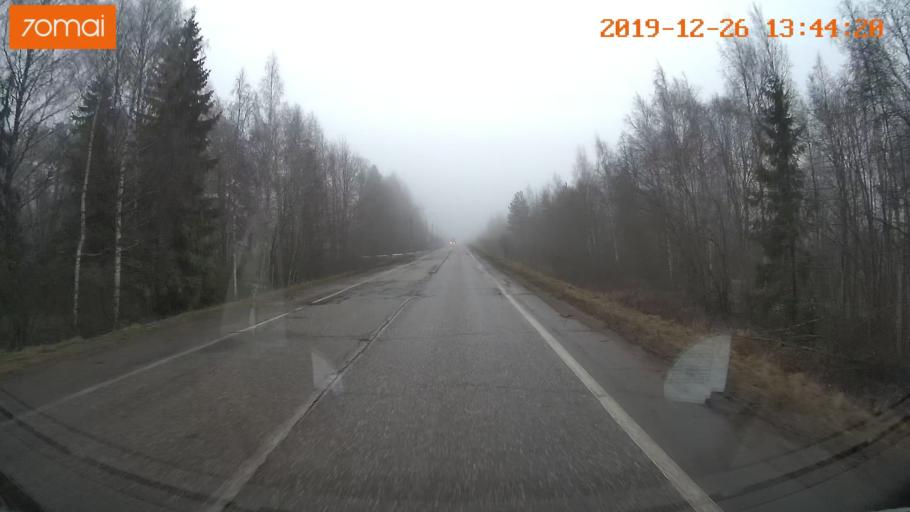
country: RU
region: Vologda
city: Sheksna
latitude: 58.7029
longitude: 38.5048
